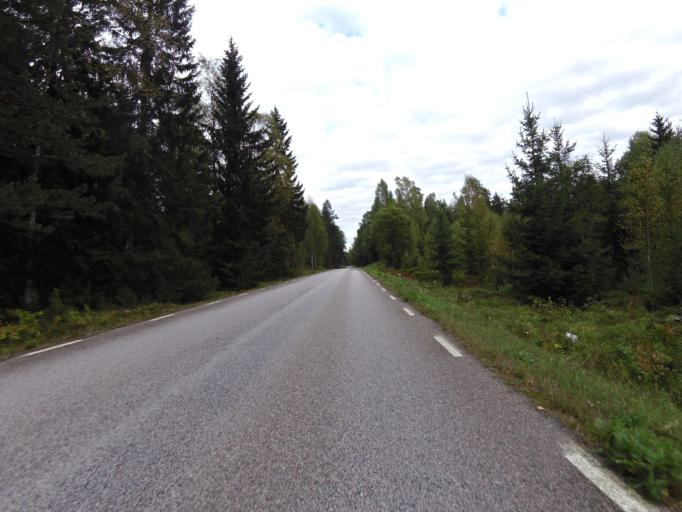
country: SE
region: Gaevleborg
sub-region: Sandvikens Kommun
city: Sandviken
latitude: 60.6666
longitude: 16.8815
